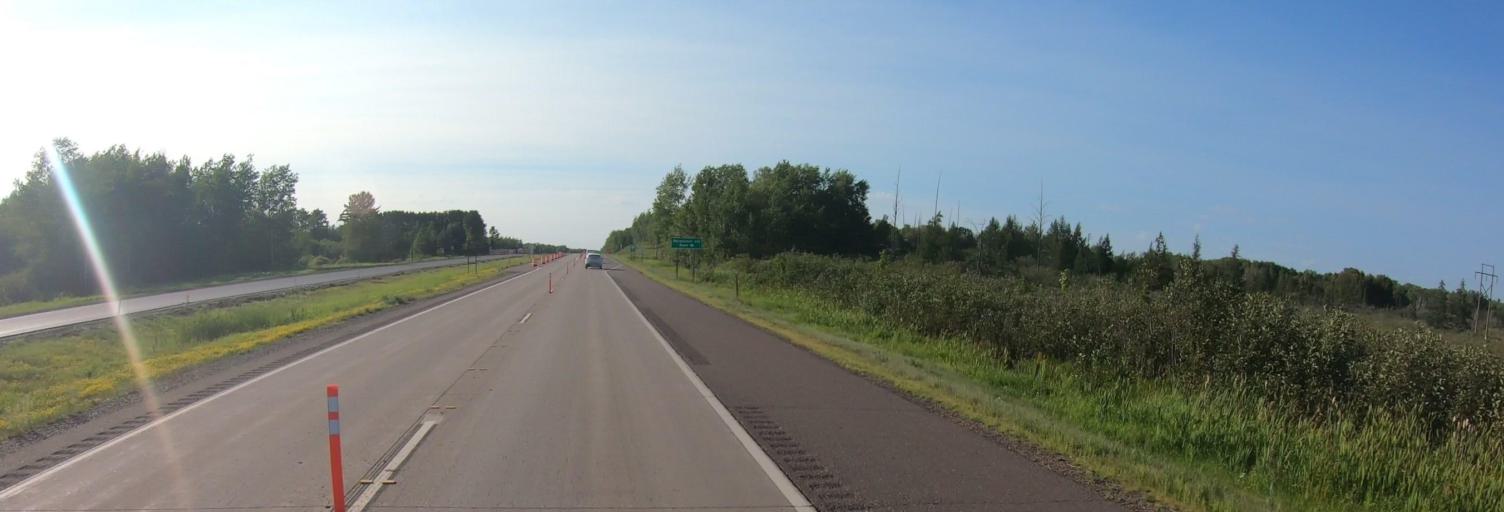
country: US
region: Minnesota
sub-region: Saint Louis County
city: Hermantown
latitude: 46.9081
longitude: -92.3855
